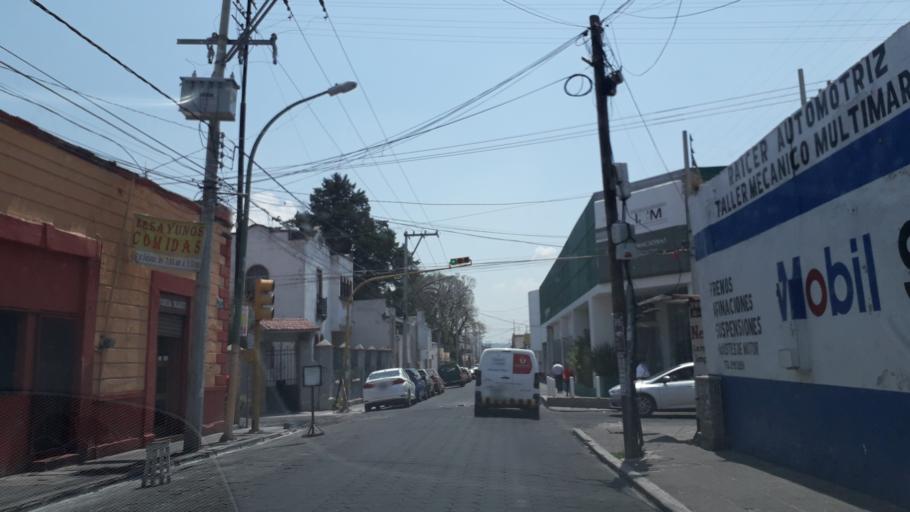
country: MX
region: Puebla
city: Puebla
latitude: 19.0521
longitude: -98.2137
